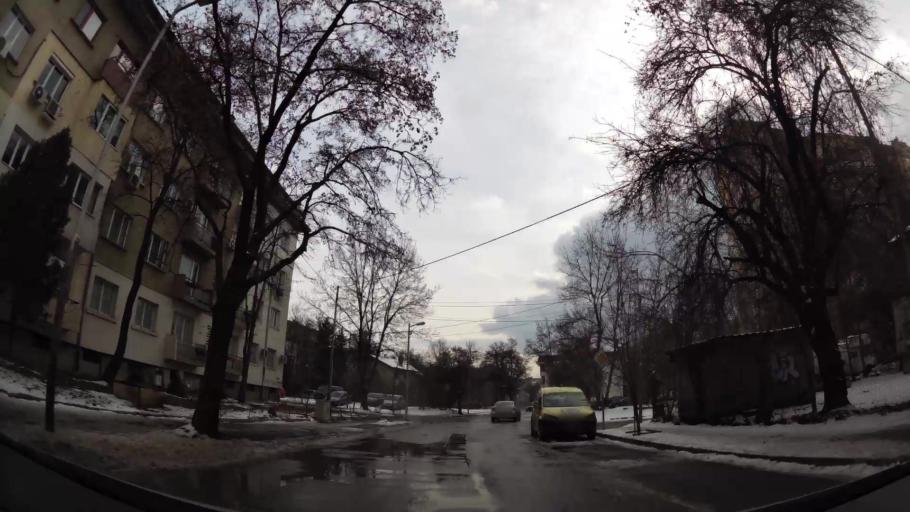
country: BG
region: Sofia-Capital
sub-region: Stolichna Obshtina
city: Sofia
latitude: 42.7028
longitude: 23.3655
